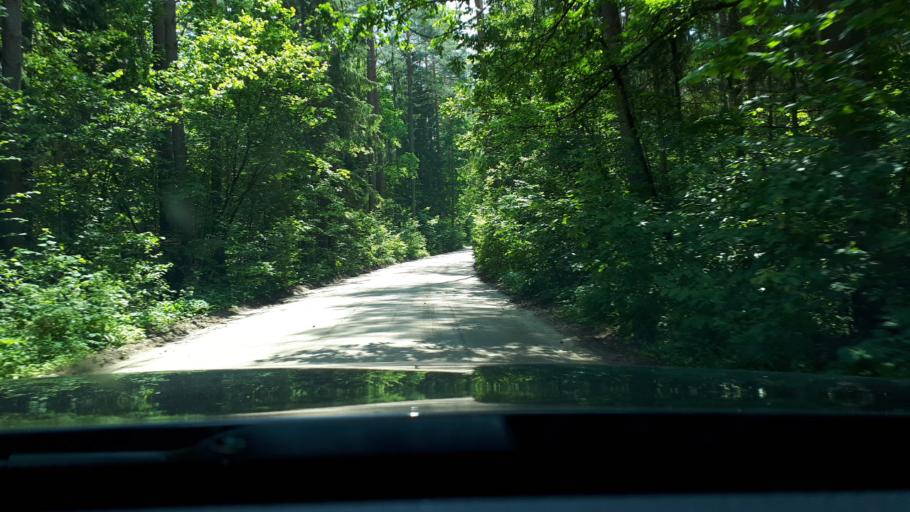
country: PL
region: Podlasie
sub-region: Powiat bialostocki
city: Suprasl
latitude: 53.2246
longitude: 23.3506
